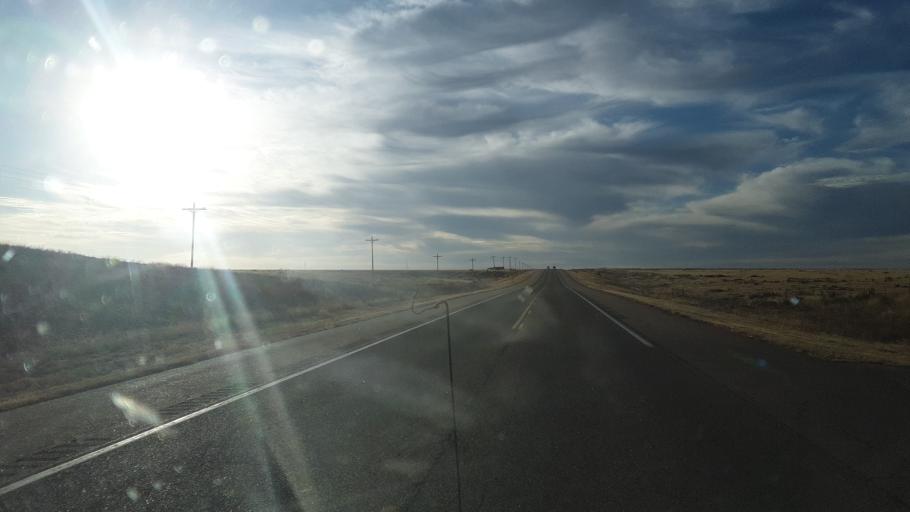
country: US
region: Kansas
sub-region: Kearny County
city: Lakin
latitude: 37.9440
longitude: -101.4508
